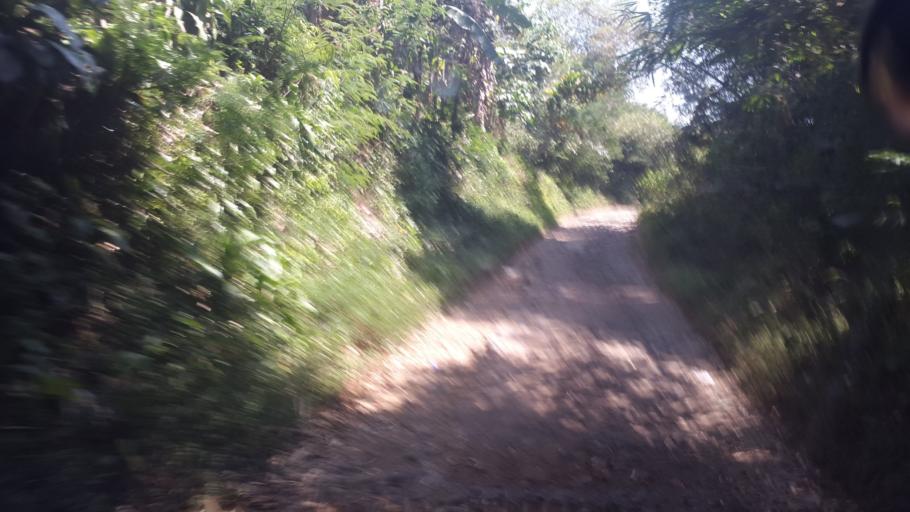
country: ID
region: West Java
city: Pasirreungit
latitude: -7.0127
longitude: 107.0160
